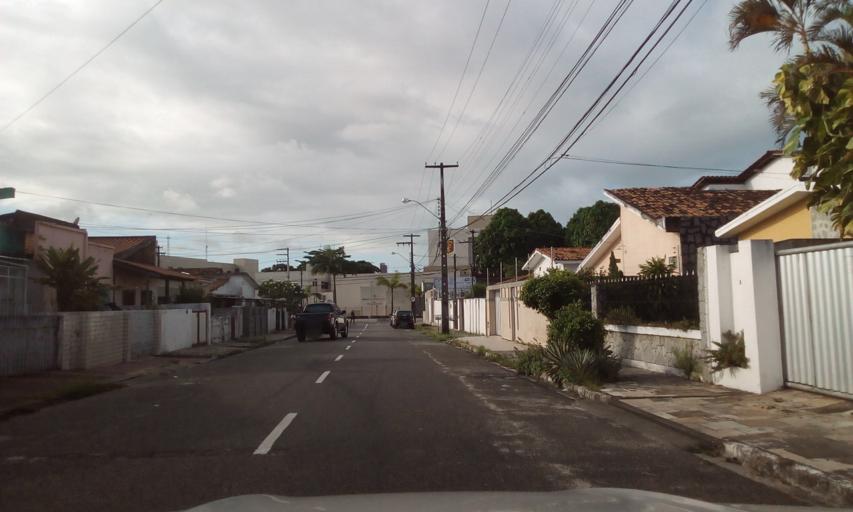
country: BR
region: Paraiba
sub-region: Joao Pessoa
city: Joao Pessoa
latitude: -7.1312
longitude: -34.8709
